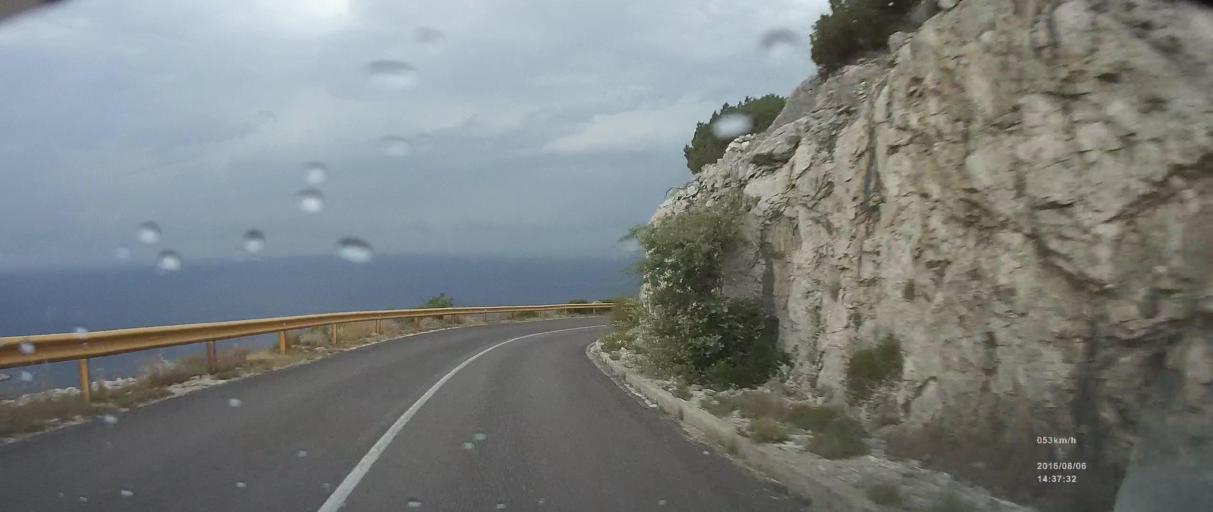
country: HR
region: Dubrovacko-Neretvanska
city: Ston
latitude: 42.7119
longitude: 17.6723
